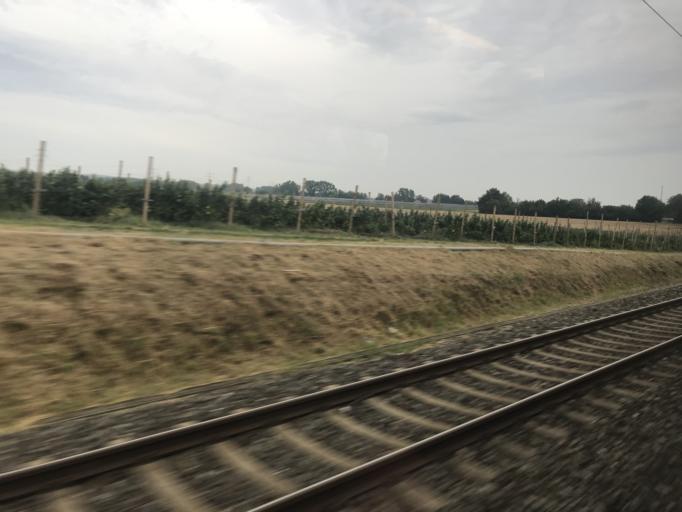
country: DE
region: Bavaria
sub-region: Regierungsbezirk Unterfranken
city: Bergtheim
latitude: 49.9034
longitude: 10.0772
